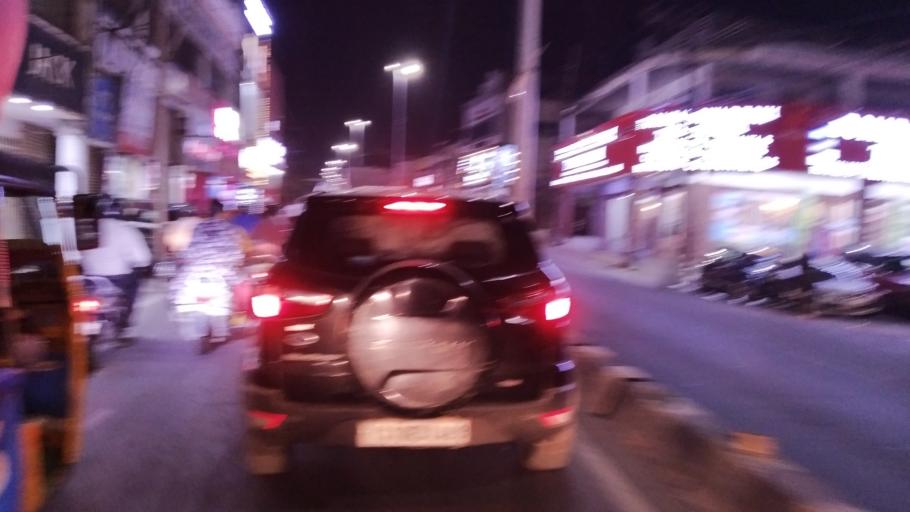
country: IN
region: Telangana
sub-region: Hyderabad
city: Malkajgiri
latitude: 17.4386
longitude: 78.4887
